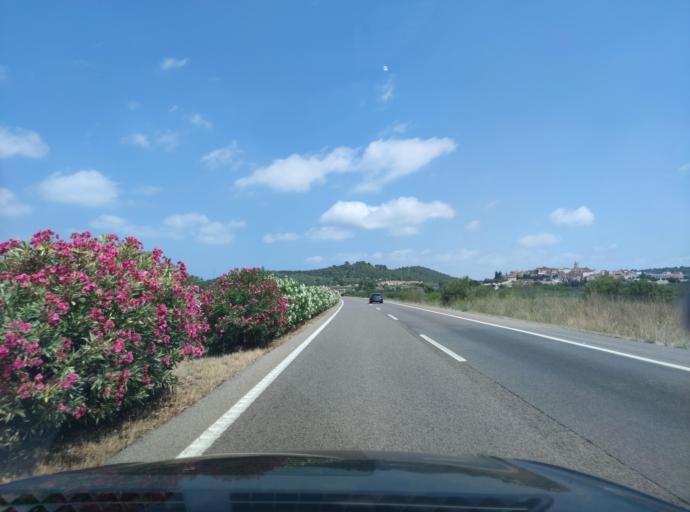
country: ES
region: Catalonia
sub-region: Provincia de Tarragona
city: Masdenverge
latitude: 40.6649
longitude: 0.5130
